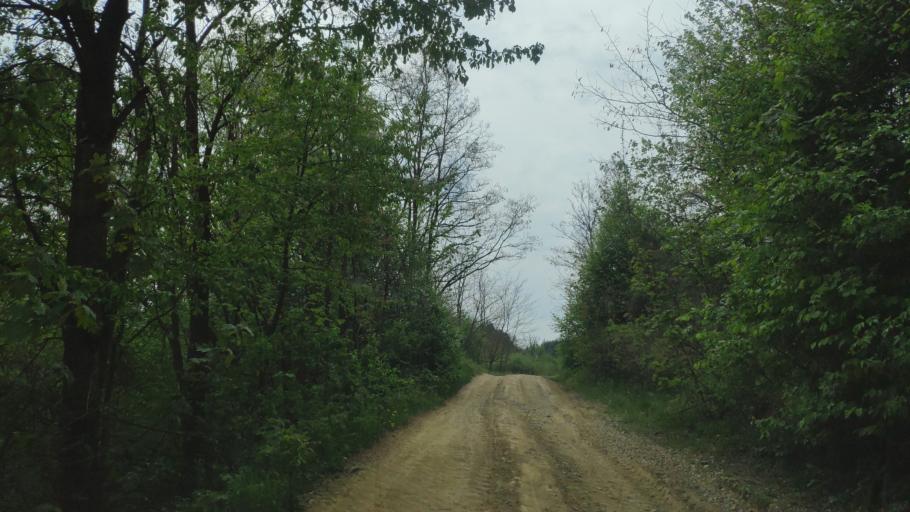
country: SK
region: Kosicky
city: Moldava nad Bodvou
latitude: 48.5646
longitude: 20.9432
